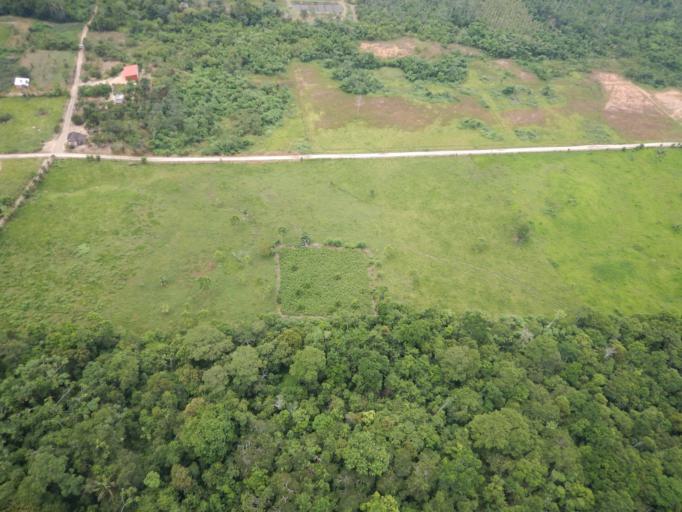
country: BO
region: Cochabamba
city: Chimore
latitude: -17.0335
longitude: -64.8380
